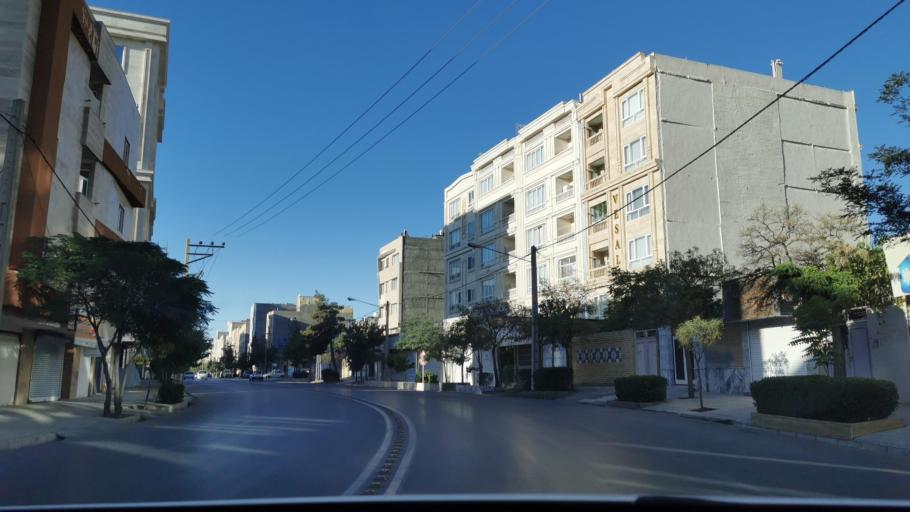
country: IR
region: Razavi Khorasan
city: Mashhad
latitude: 36.3578
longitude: 59.4973
